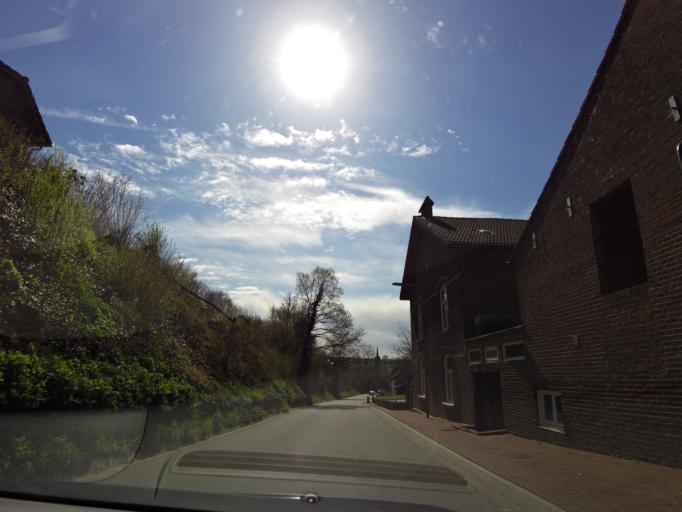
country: NL
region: Limburg
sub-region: Gemeente Voerendaal
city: Ubachsberg
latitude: 50.8283
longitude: 5.9347
